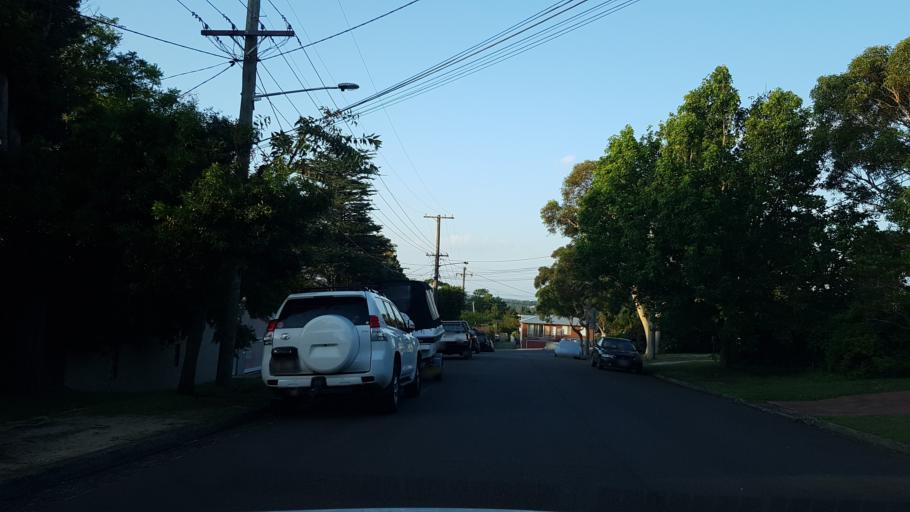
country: AU
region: New South Wales
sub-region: Warringah
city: Narrabeen
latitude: -33.7276
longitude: 151.2832
